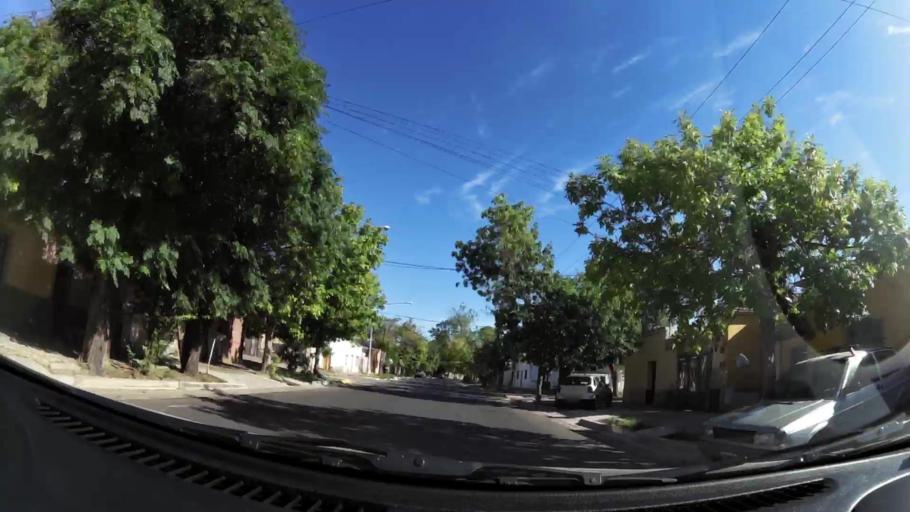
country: AR
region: Mendoza
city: Mendoza
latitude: -32.9072
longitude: -68.8330
